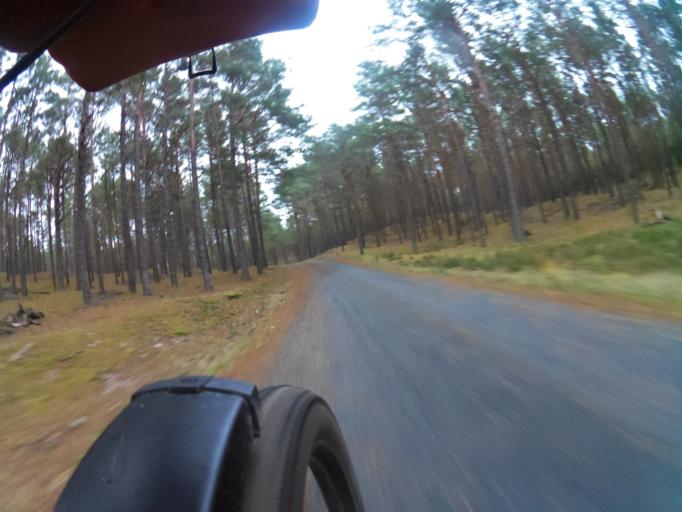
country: PL
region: Pomeranian Voivodeship
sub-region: Powiat wejherowski
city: Choczewo
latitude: 54.7885
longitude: 17.7533
